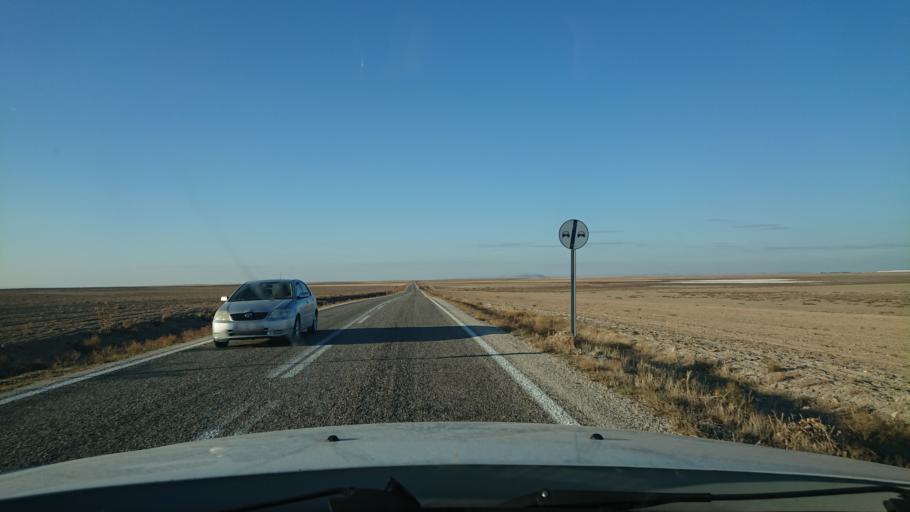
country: TR
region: Konya
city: Cihanbeyli
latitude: 38.7025
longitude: 33.1054
